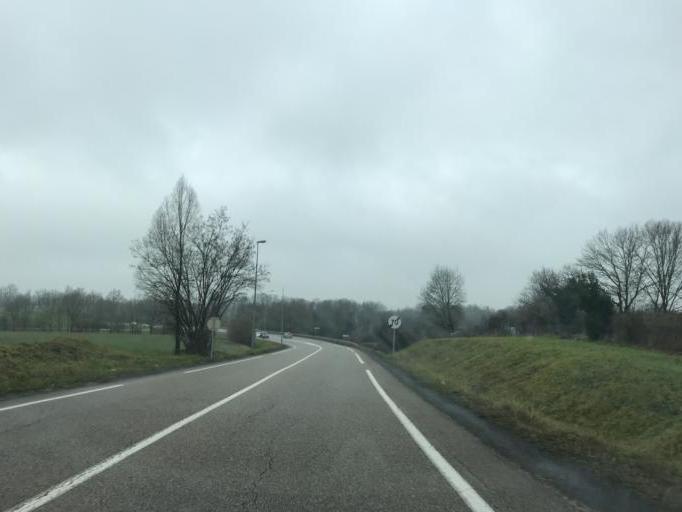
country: FR
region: Rhone-Alpes
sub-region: Departement de l'Ain
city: Peronnas
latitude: 46.1897
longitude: 5.1960
